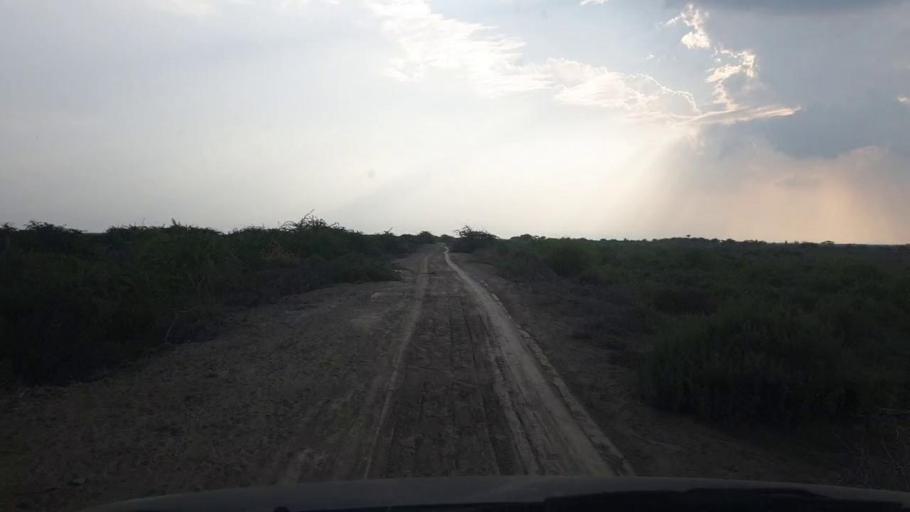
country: PK
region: Sindh
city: Badin
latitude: 24.4703
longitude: 68.6964
